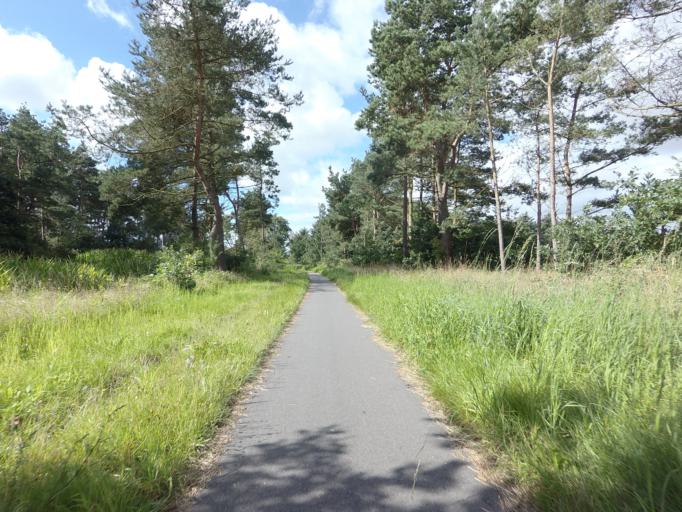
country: DK
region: Central Jutland
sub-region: Silkeborg Kommune
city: Svejbaek
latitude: 56.2100
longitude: 9.6734
